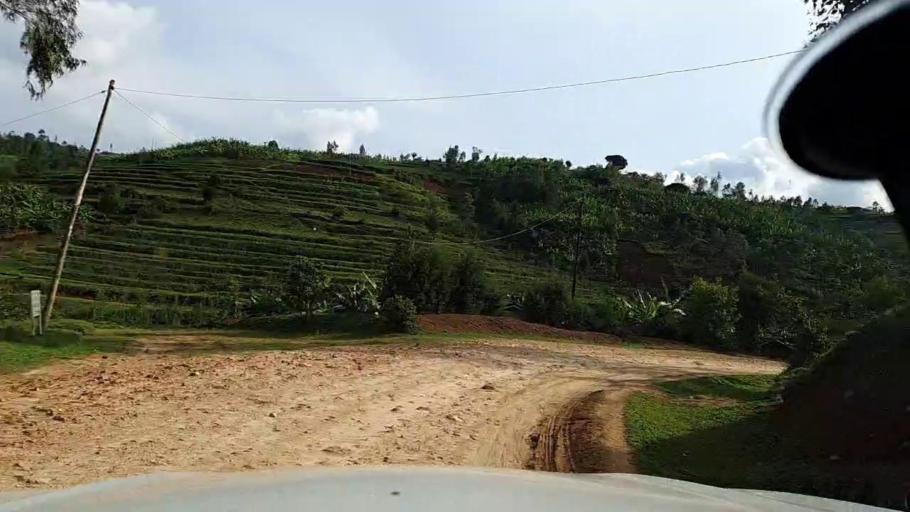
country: RW
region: Southern Province
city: Gitarama
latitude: -2.1668
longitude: 29.5584
